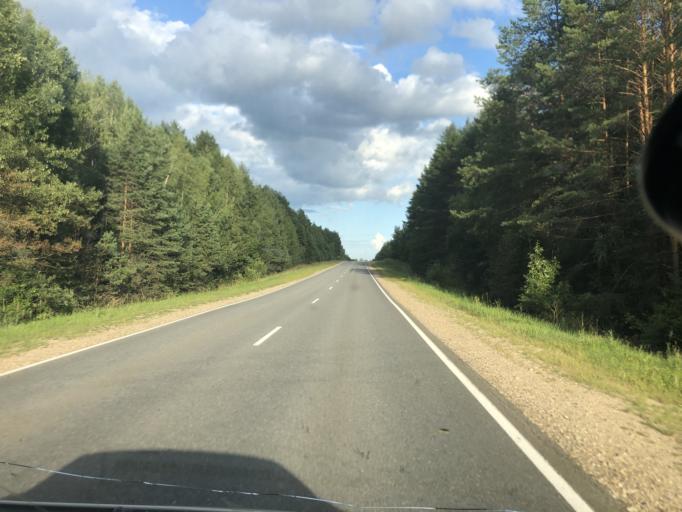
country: RU
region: Kaluga
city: Yukhnov
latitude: 54.7105
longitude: 35.2527
